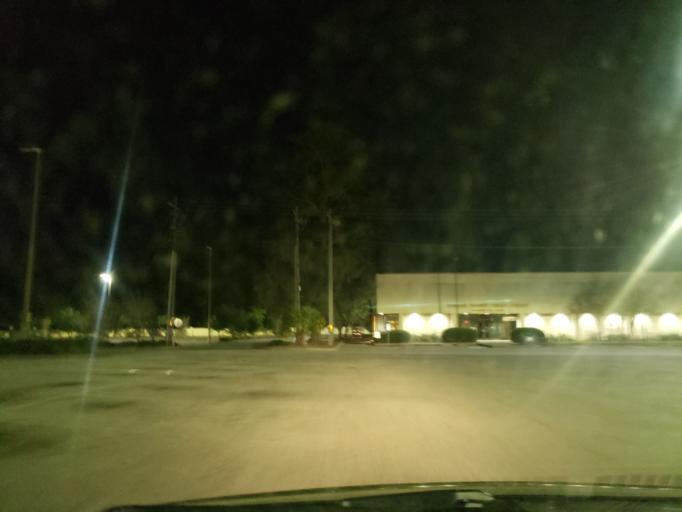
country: US
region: Georgia
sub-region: Chatham County
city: Isle of Hope
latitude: 32.0012
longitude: -81.1182
